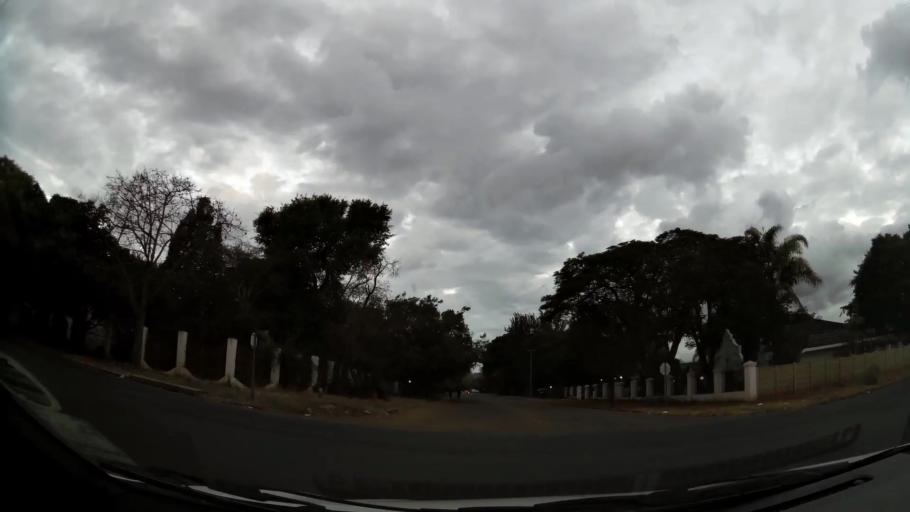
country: ZA
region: Limpopo
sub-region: Waterberg District Municipality
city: Mokopane
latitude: -24.1877
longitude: 28.9979
